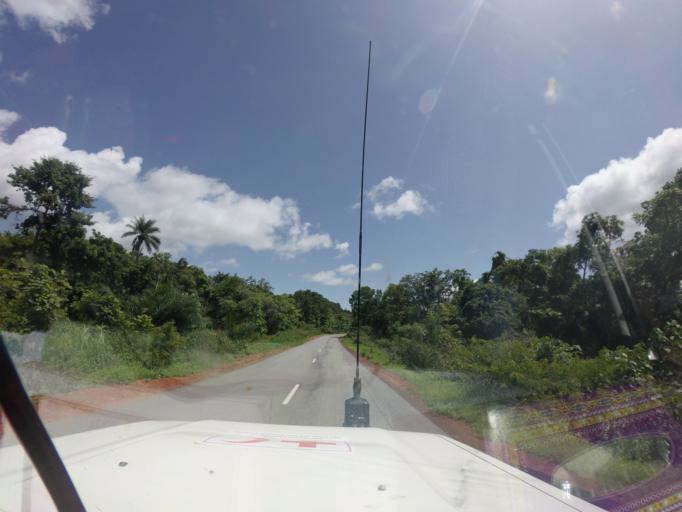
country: GN
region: Mamou
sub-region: Mamou Prefecture
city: Mamou
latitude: 10.1889
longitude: -11.7670
